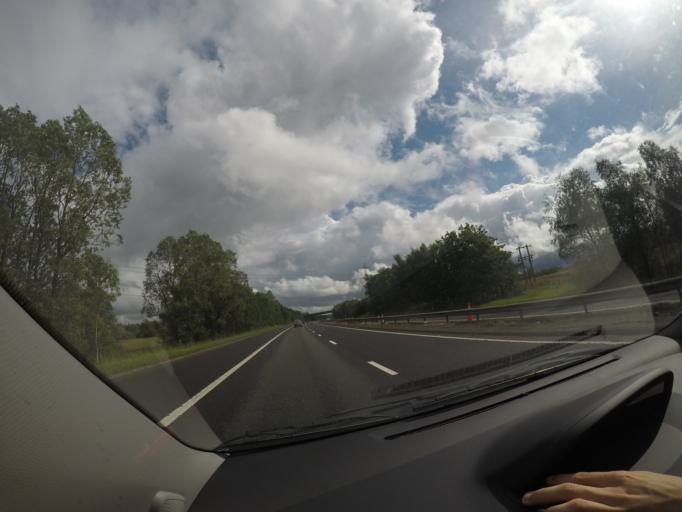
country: GB
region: Scotland
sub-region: North Lanarkshire
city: Chryston
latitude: 55.8773
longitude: -4.0800
